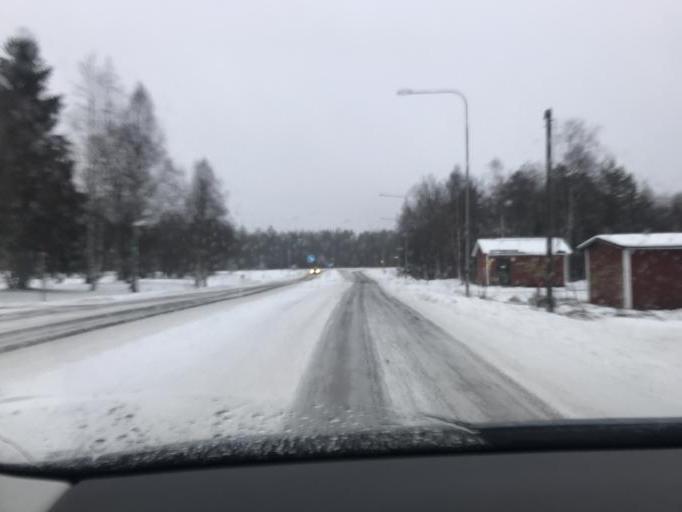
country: SE
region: Norrbotten
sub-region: Lulea Kommun
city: Sodra Sunderbyn
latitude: 65.6541
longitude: 21.9666
